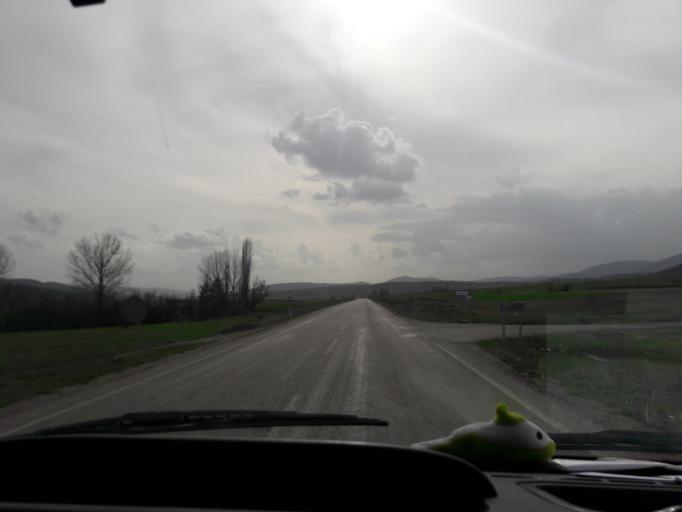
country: TR
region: Gumushane
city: Siran
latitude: 40.1620
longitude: 39.0345
